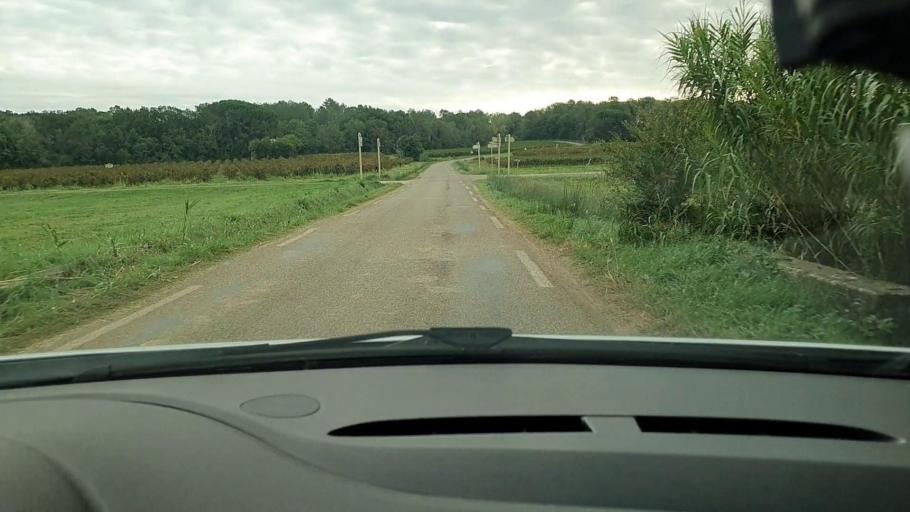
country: FR
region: Languedoc-Roussillon
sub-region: Departement du Gard
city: Moussac
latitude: 44.0342
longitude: 4.2598
